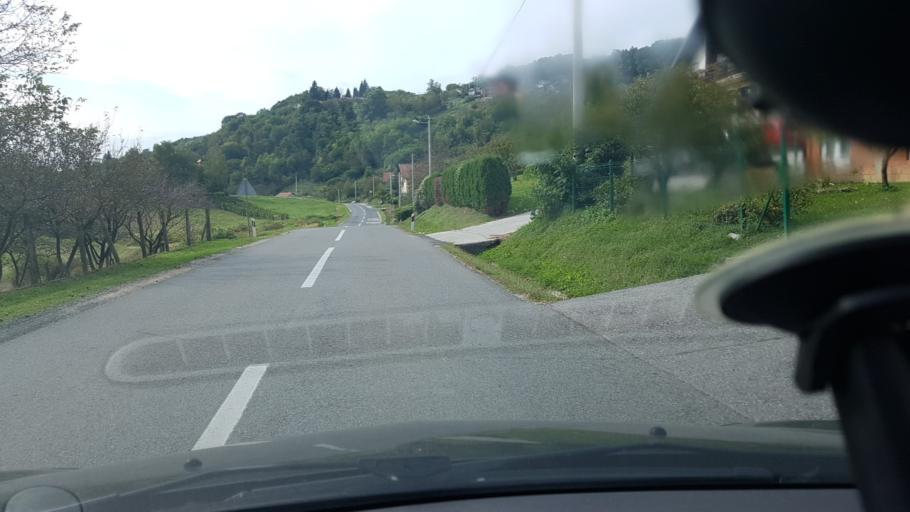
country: HR
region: Varazdinska
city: Remetinec
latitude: 46.1622
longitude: 16.2959
